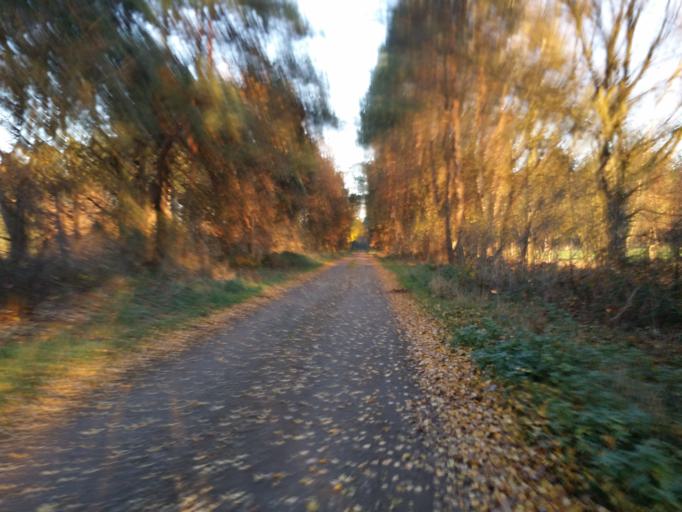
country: DE
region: Lower Saxony
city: Hellwege
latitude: 53.0728
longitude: 9.2638
